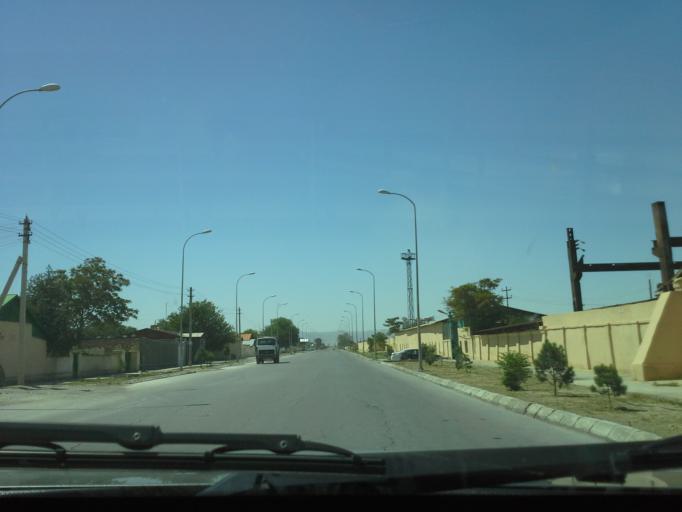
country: TM
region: Balkan
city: Serdar
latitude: 38.9775
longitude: 56.2707
